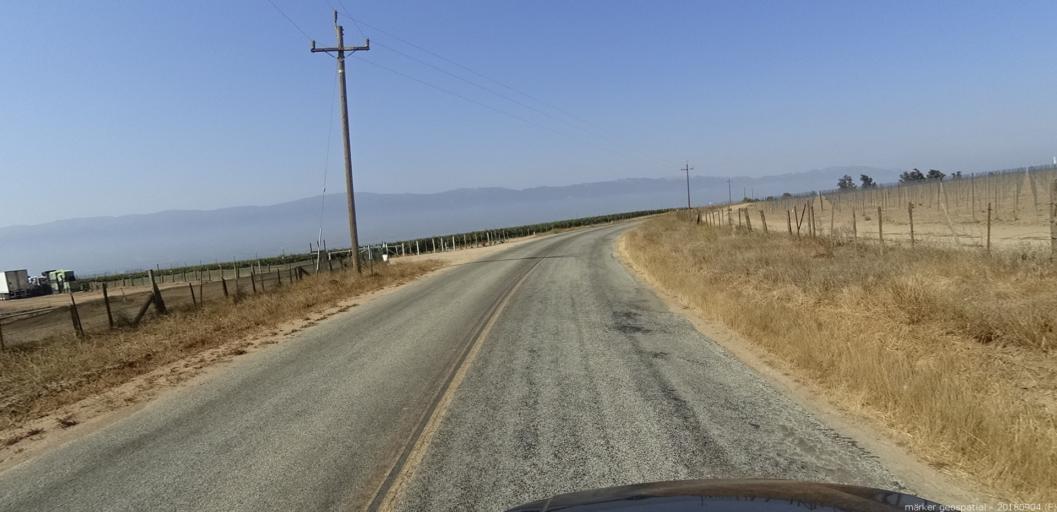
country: US
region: California
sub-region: Monterey County
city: Gonzales
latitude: 36.5041
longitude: -121.3736
